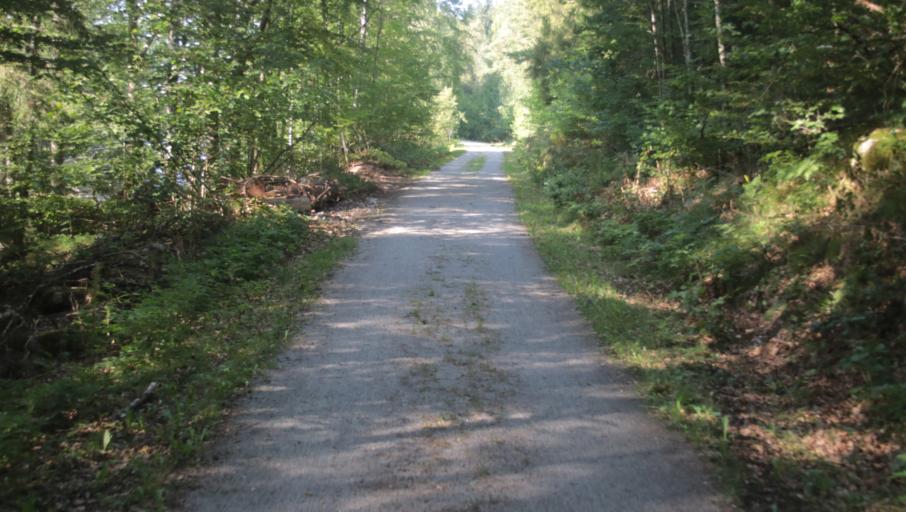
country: SE
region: Blekinge
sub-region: Karlshamns Kommun
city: Svangsta
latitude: 56.3728
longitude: 14.6822
